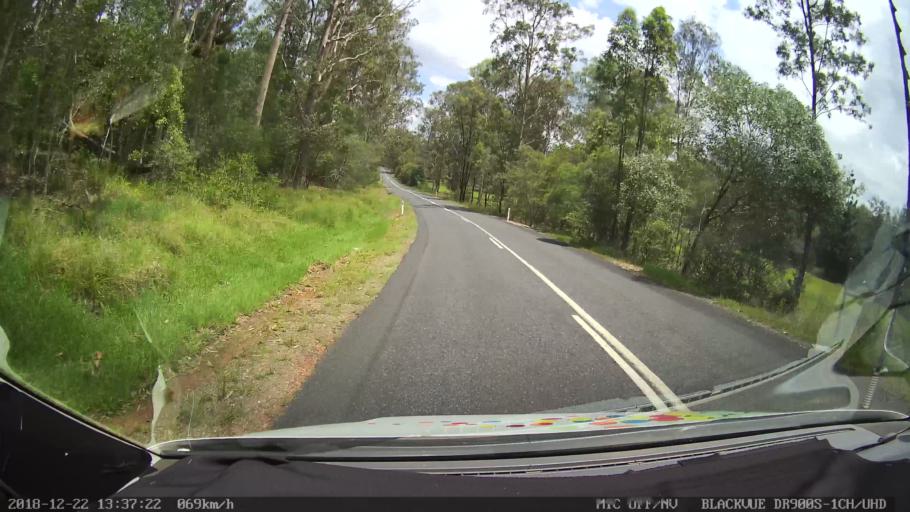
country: AU
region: New South Wales
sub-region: Clarence Valley
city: Coutts Crossing
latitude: -29.8890
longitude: 152.7877
